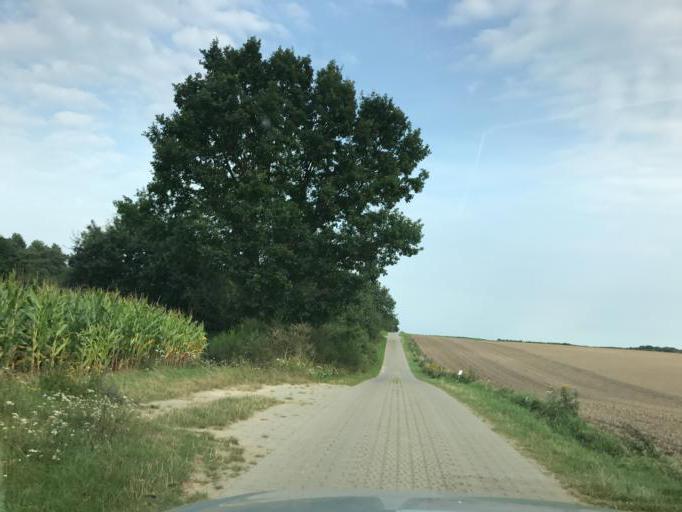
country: DE
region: Mecklenburg-Vorpommern
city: Rechlin
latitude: 53.3284
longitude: 12.7458
